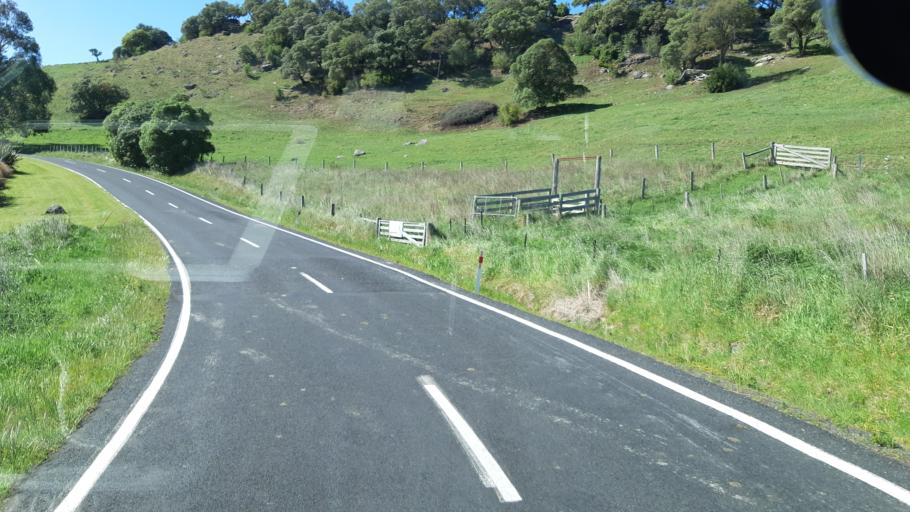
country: NZ
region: Otago
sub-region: Dunedin City
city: Portobello
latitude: -45.6583
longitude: 170.6419
